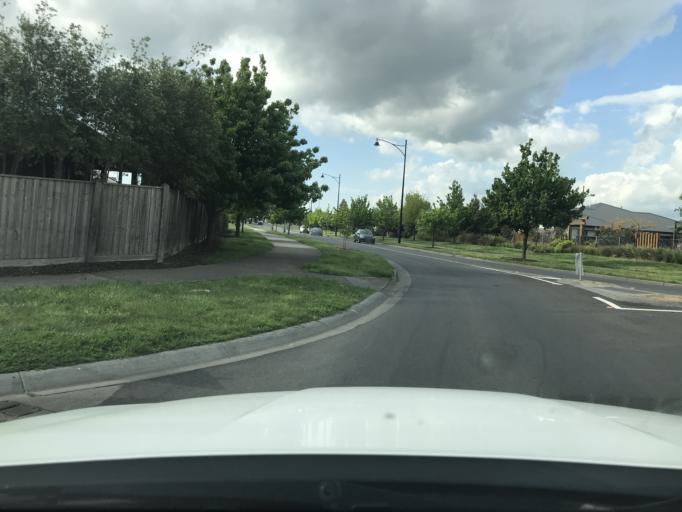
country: AU
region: Victoria
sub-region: Hume
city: Roxburgh Park
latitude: -37.5869
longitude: 144.9062
